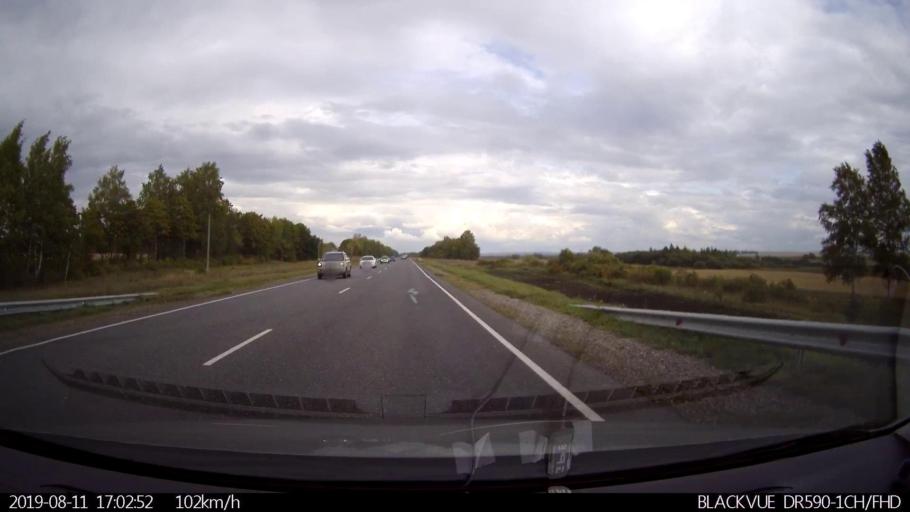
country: RU
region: Ulyanovsk
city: Mayna
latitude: 54.3047
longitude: 47.7255
